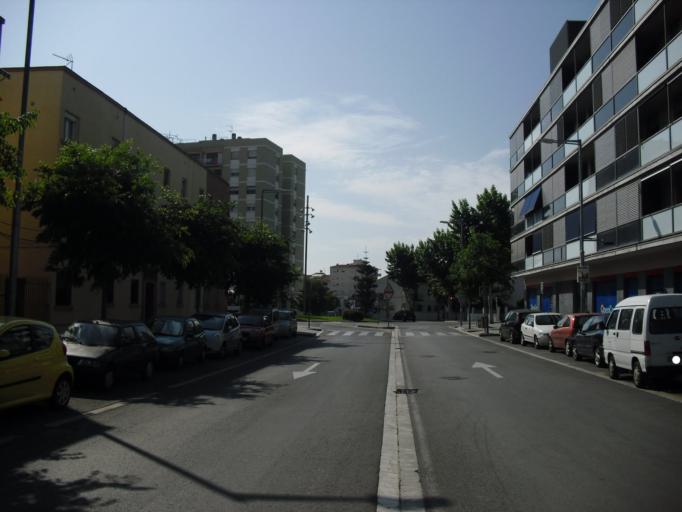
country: ES
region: Catalonia
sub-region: Provincia de Barcelona
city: Vilanova i la Geltru
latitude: 41.2256
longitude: 1.7324
